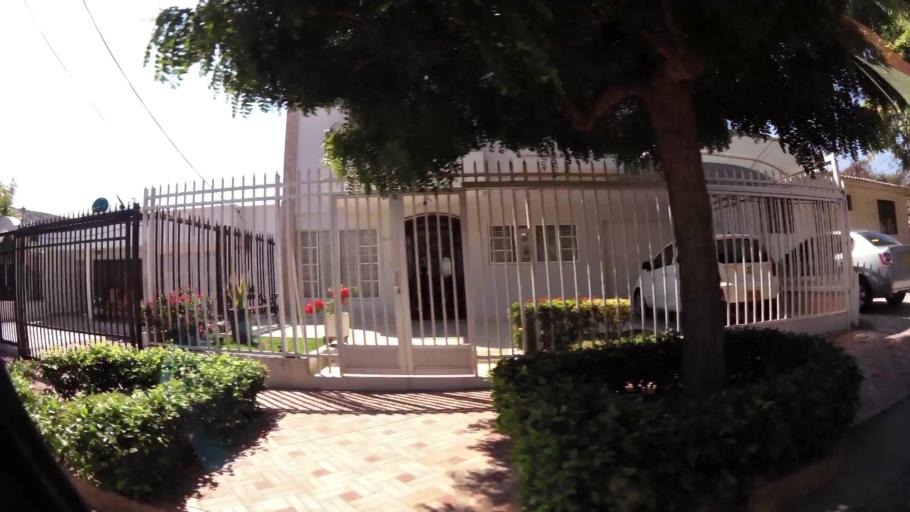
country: CO
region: Atlantico
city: Barranquilla
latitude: 11.0168
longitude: -74.8049
